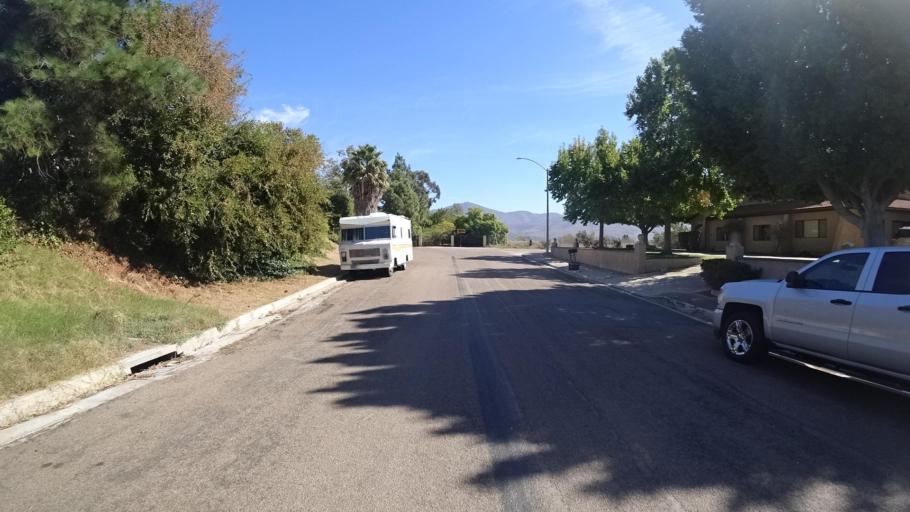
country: US
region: California
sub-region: San Diego County
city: La Presa
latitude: 32.7006
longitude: -117.0025
